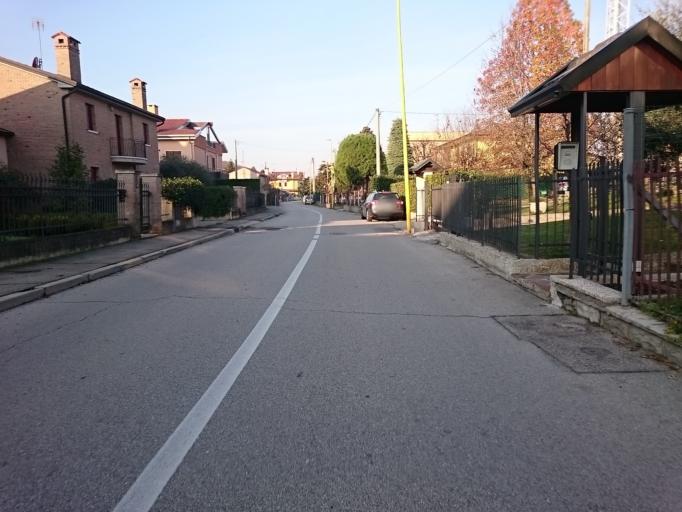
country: IT
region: Veneto
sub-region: Provincia di Padova
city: Ponte San Nicolo
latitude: 45.3693
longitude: 11.9198
